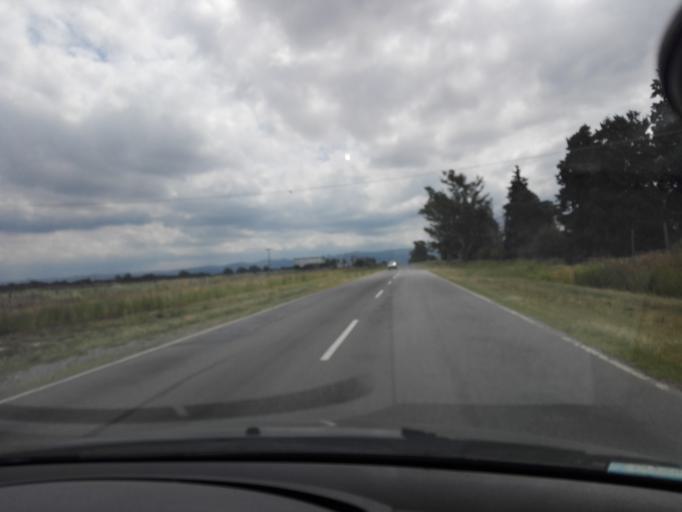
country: AR
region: Cordoba
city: Alta Gracia
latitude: -31.6581
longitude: -64.3687
